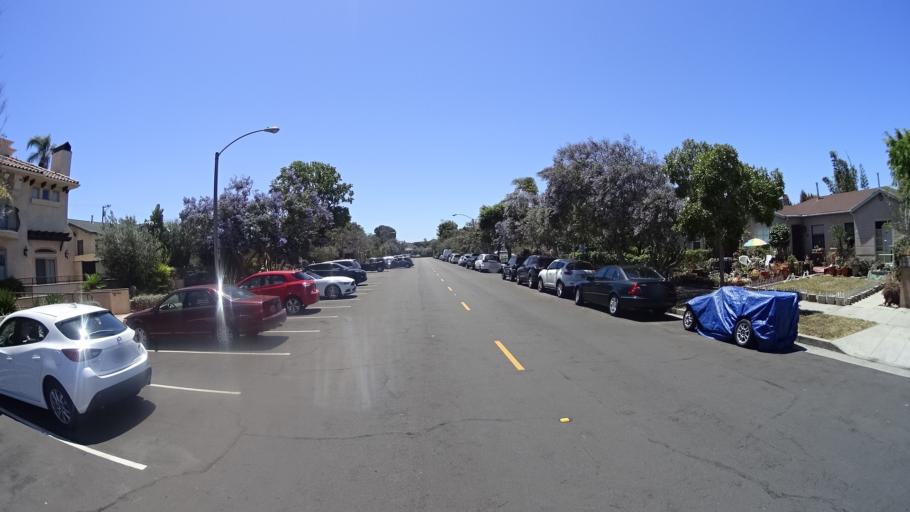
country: US
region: California
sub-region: Los Angeles County
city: Santa Monica
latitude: 34.0160
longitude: -118.4799
